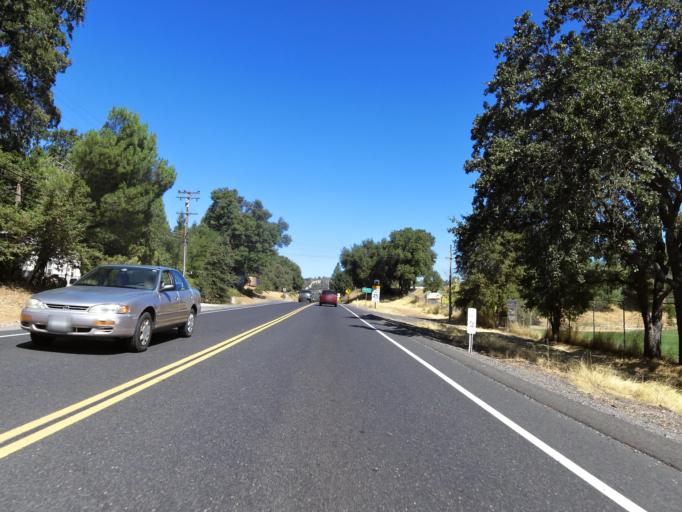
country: US
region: California
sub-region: Calaveras County
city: Murphys
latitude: 38.1308
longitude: -120.4542
